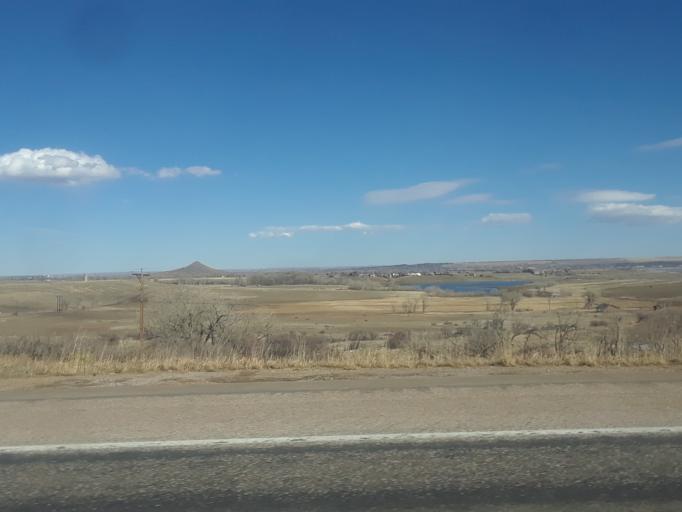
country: US
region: Colorado
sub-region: Boulder County
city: Boulder
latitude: 40.1037
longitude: -105.2822
